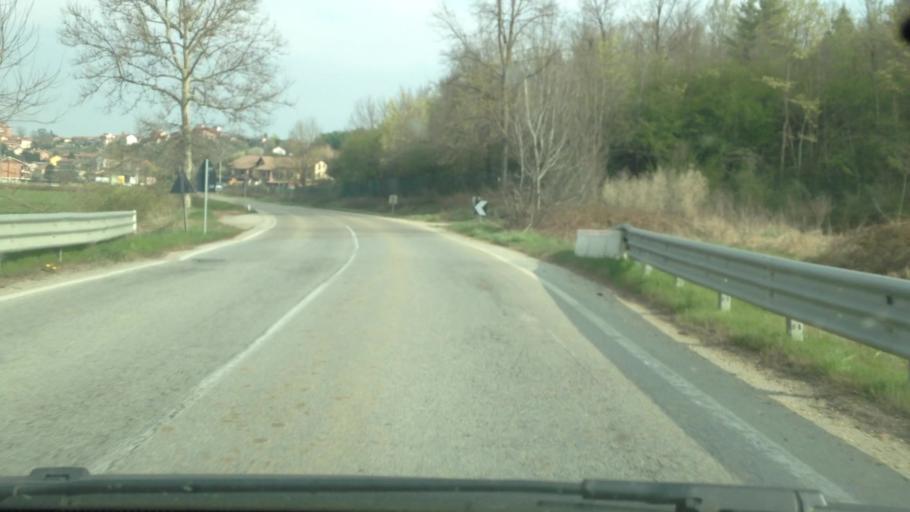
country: IT
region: Piedmont
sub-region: Provincia di Torino
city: Pralormo
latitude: 44.8525
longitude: 7.9085
